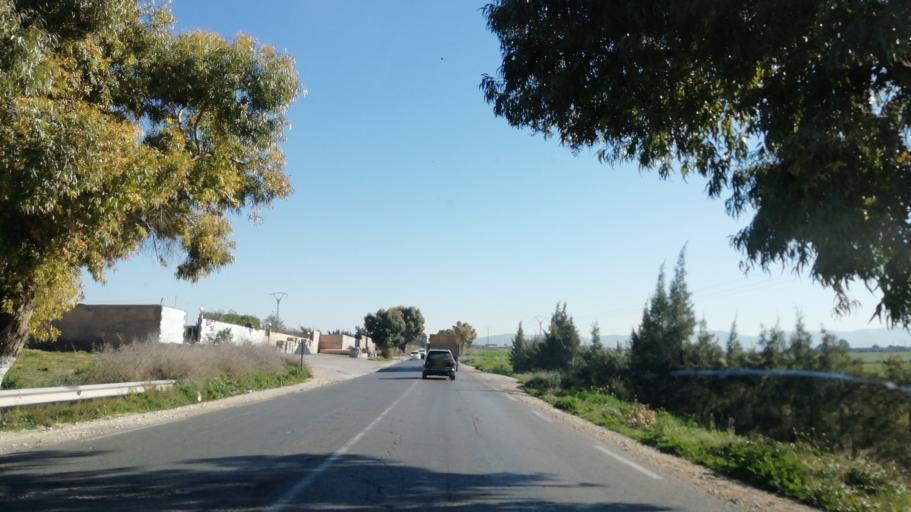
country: DZ
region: Relizane
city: Zemoura
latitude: 35.7540
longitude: 0.6817
